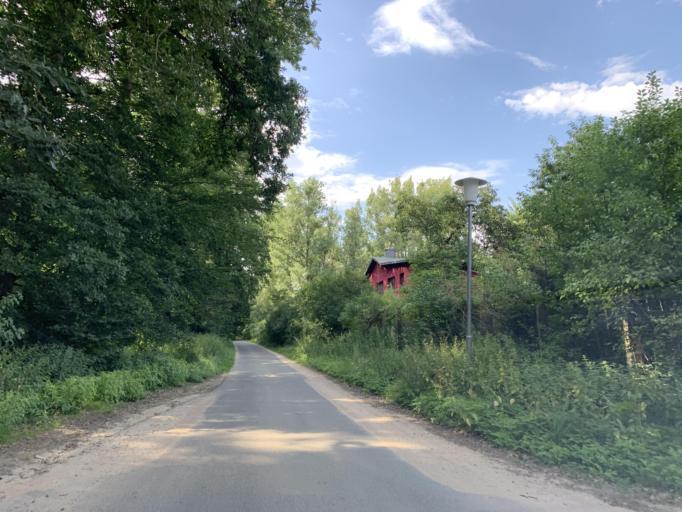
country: DE
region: Mecklenburg-Vorpommern
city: Carpin
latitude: 53.3782
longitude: 13.2223
